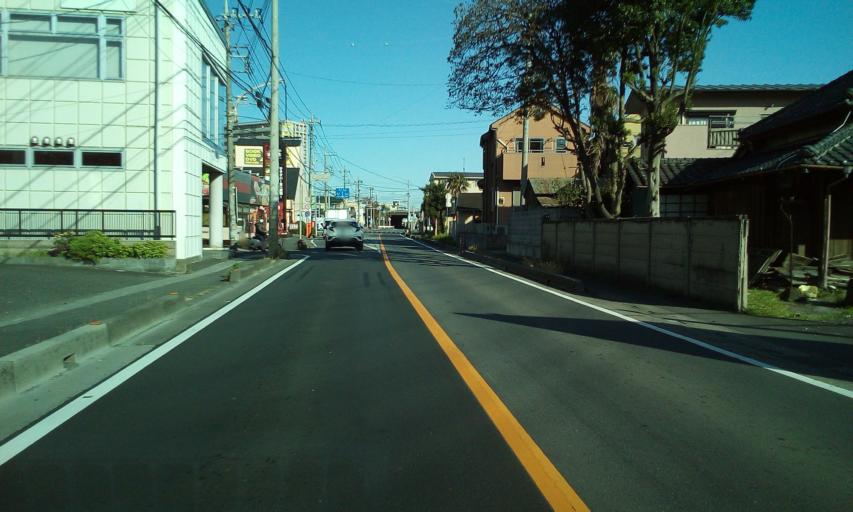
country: JP
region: Chiba
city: Nagareyama
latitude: 35.8448
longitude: 139.8809
